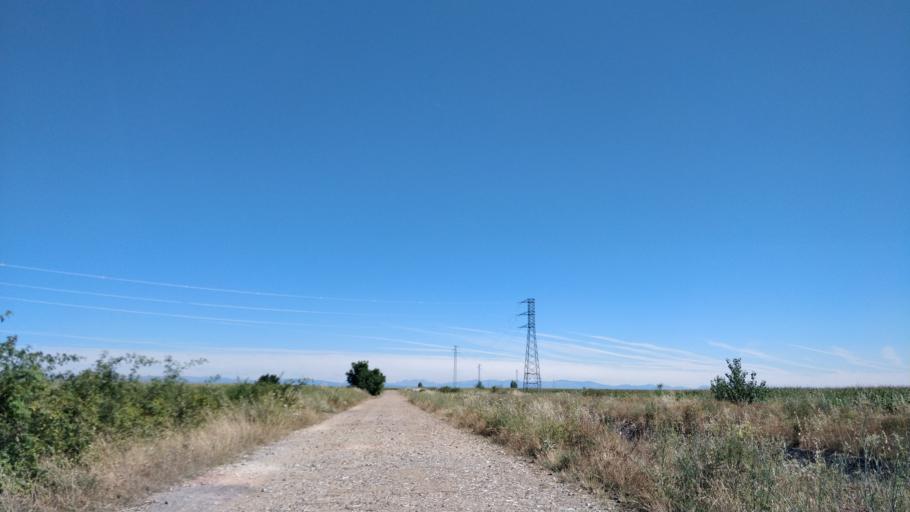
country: ES
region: Castille and Leon
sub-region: Provincia de Leon
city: Bustillo del Paramo
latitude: 42.4284
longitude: -5.8216
